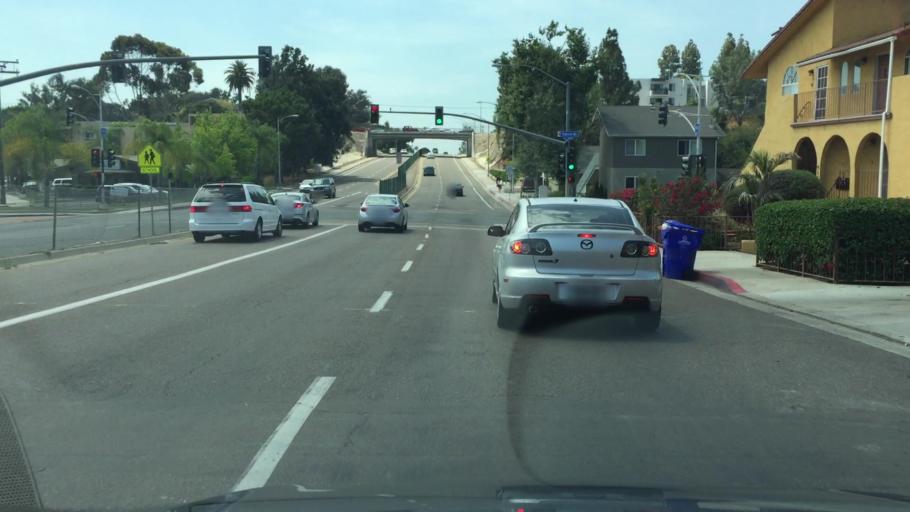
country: US
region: California
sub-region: San Diego County
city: Lemon Grove
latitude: 32.7553
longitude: -117.0795
